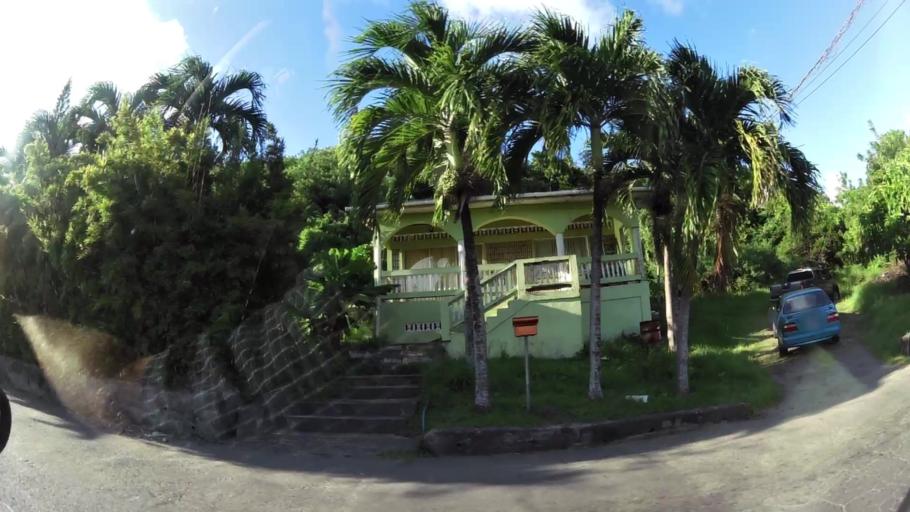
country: TT
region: Tobago
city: Scarborough
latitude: 11.1828
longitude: -60.7004
